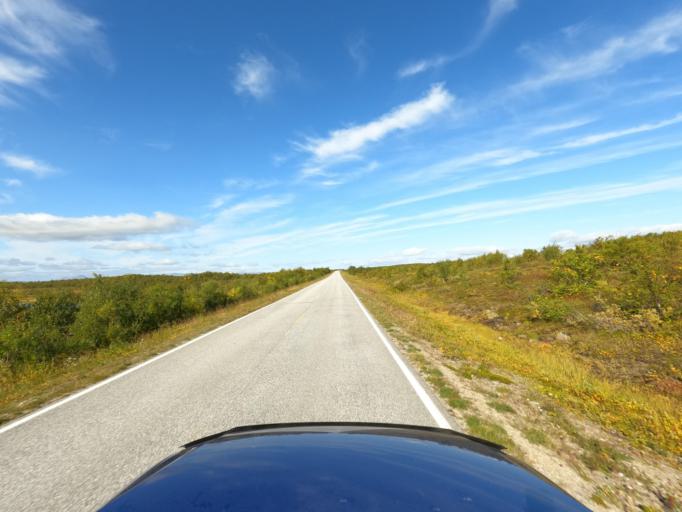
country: NO
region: Finnmark Fylke
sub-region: Karasjok
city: Karasjohka
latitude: 69.7055
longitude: 25.2496
